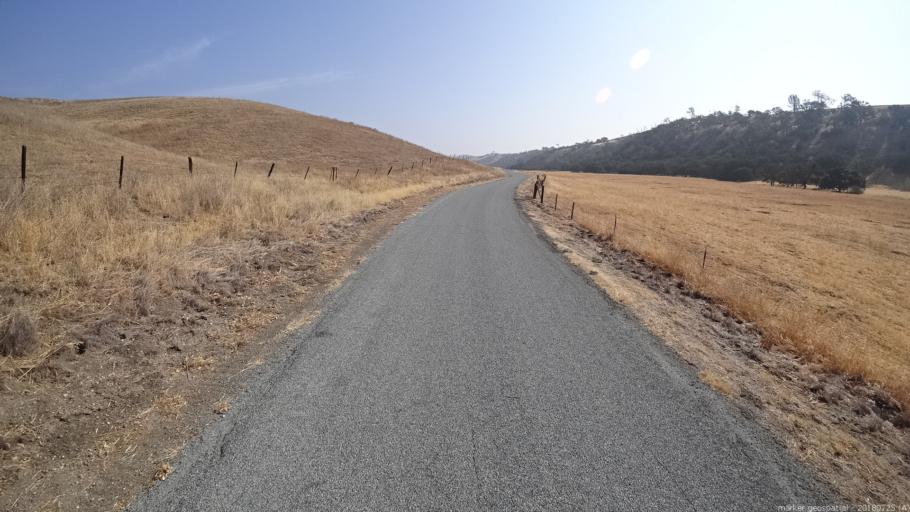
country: US
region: California
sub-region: San Luis Obispo County
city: San Miguel
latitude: 35.8107
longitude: -120.5282
